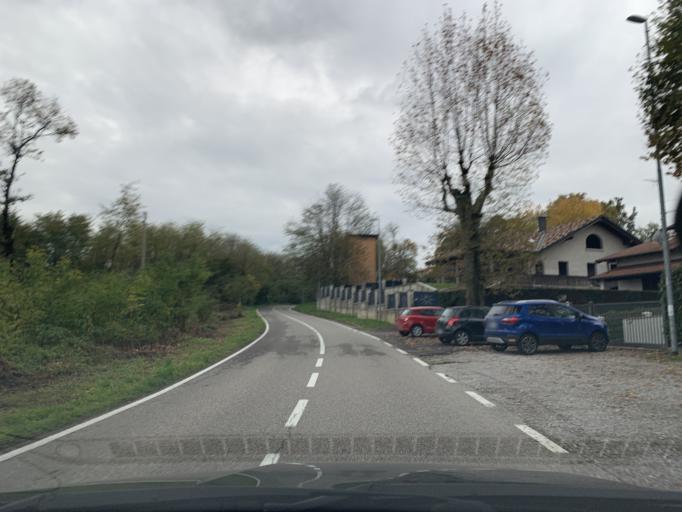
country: IT
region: Lombardy
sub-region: Provincia di Como
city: Casnate Con Bernate
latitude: 45.7509
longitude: 9.0708
